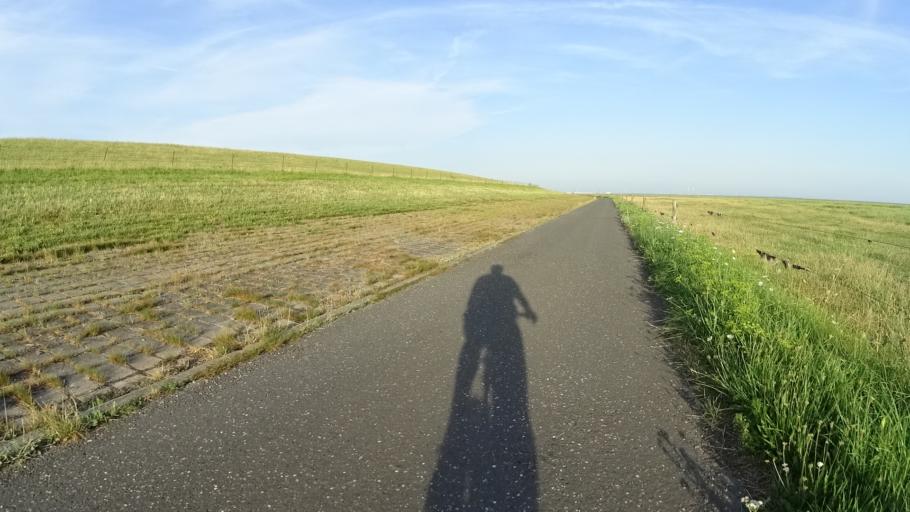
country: DE
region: Lower Saxony
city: Butjadingen
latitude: 53.6085
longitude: 8.2920
